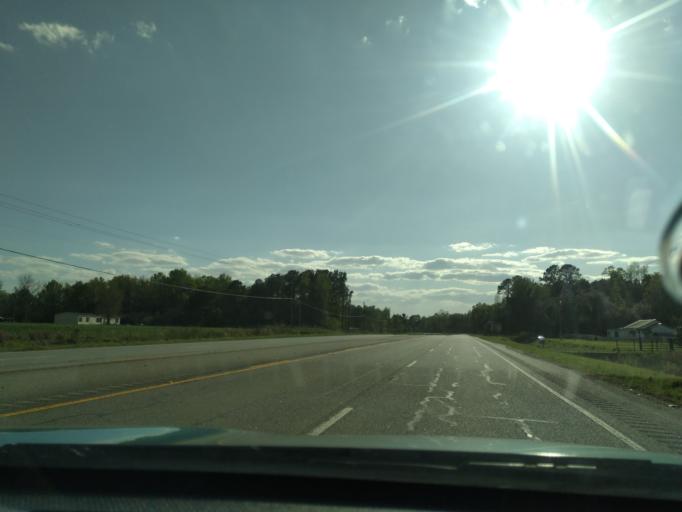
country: US
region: South Carolina
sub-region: Williamsburg County
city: Kingstree
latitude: 33.6372
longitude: -79.9104
